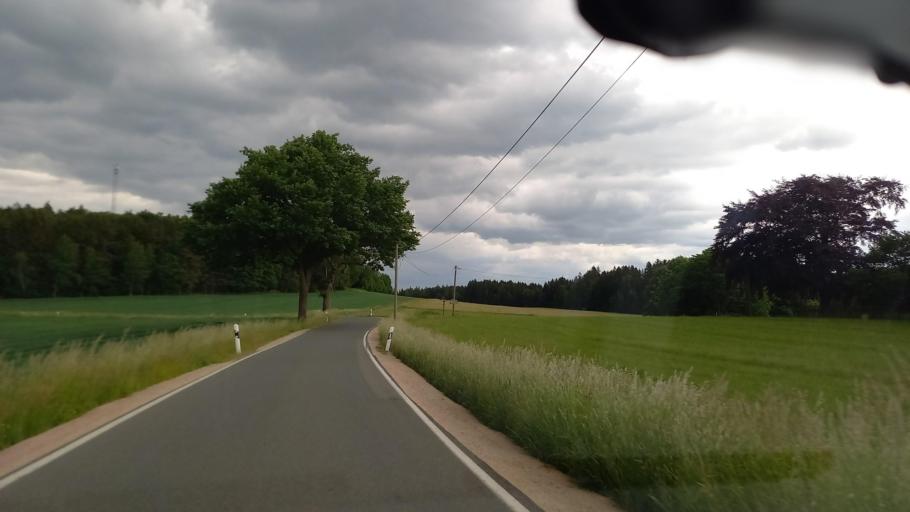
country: DE
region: Saxony
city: Rodewisch
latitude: 50.5586
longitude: 12.4550
